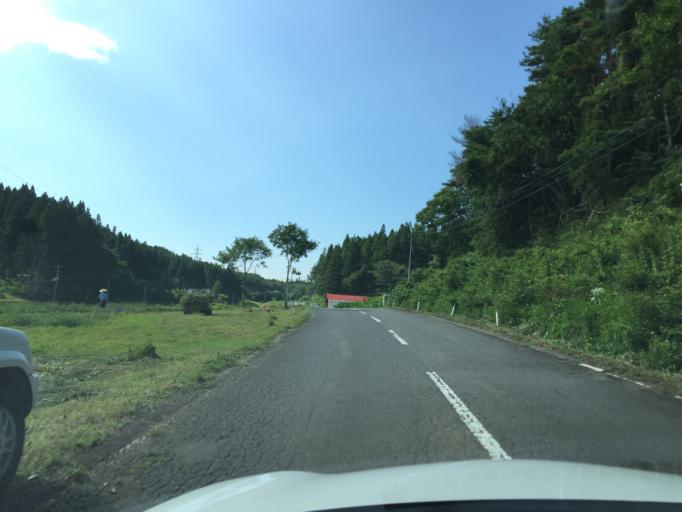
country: JP
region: Fukushima
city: Ishikawa
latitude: 37.1494
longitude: 140.6347
